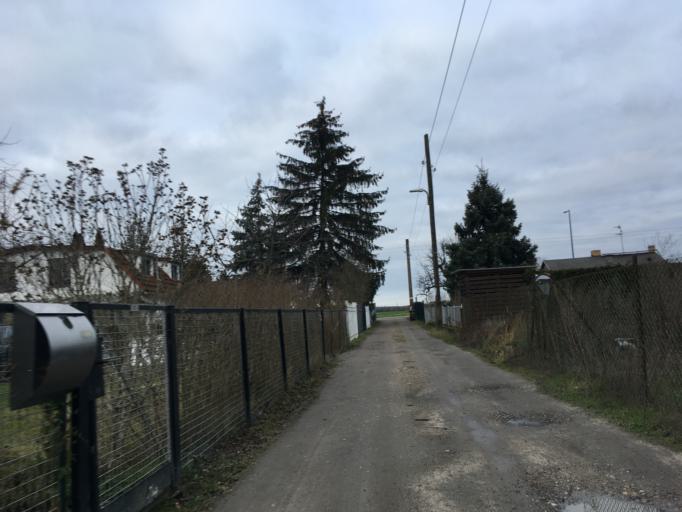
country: DE
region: Berlin
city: Niederschonhausen
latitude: 52.6033
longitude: 13.4088
